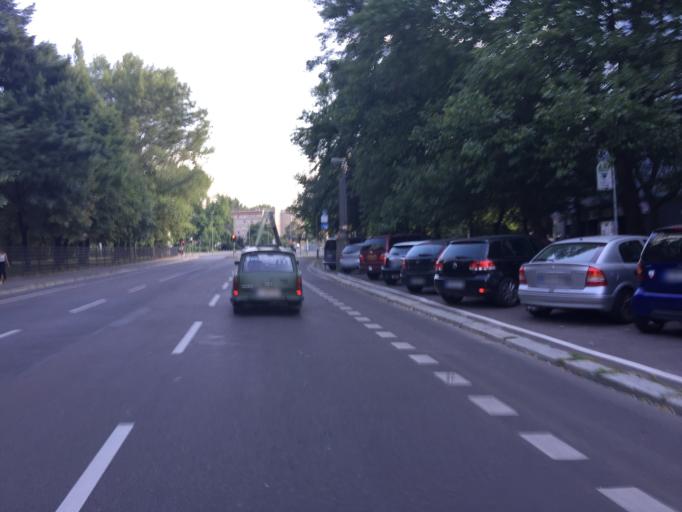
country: DE
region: Berlin
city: Friedrichshain Bezirk
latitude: 52.5150
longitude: 13.4401
